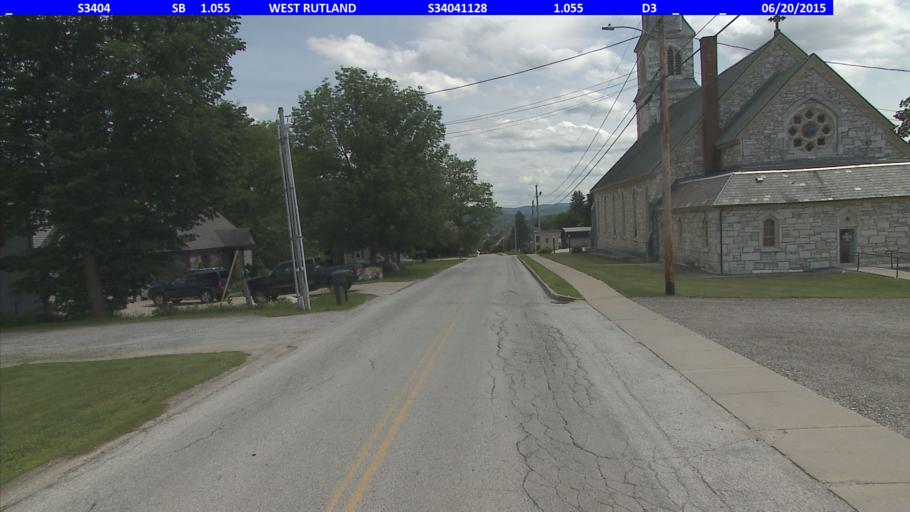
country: US
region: Vermont
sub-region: Rutland County
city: West Rutland
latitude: 43.6067
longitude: -73.0485
